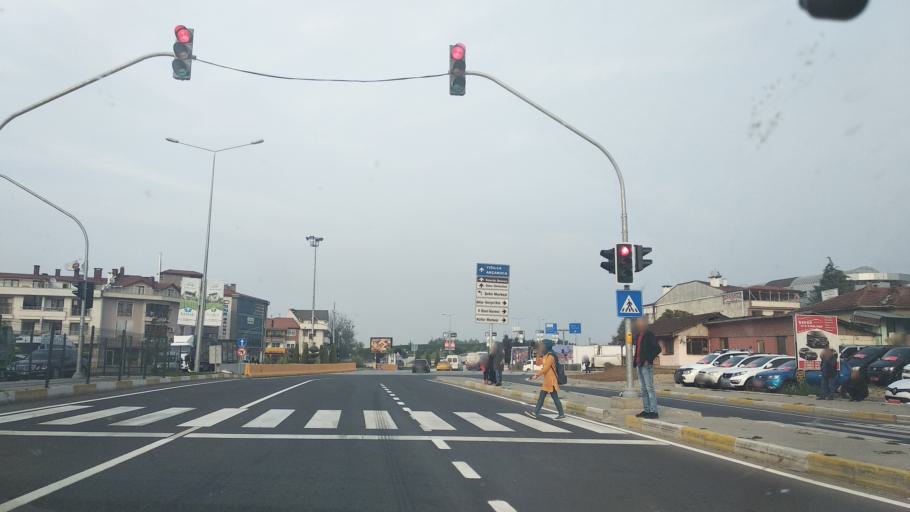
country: TR
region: Duzce
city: Duzce
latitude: 40.8352
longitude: 31.1707
